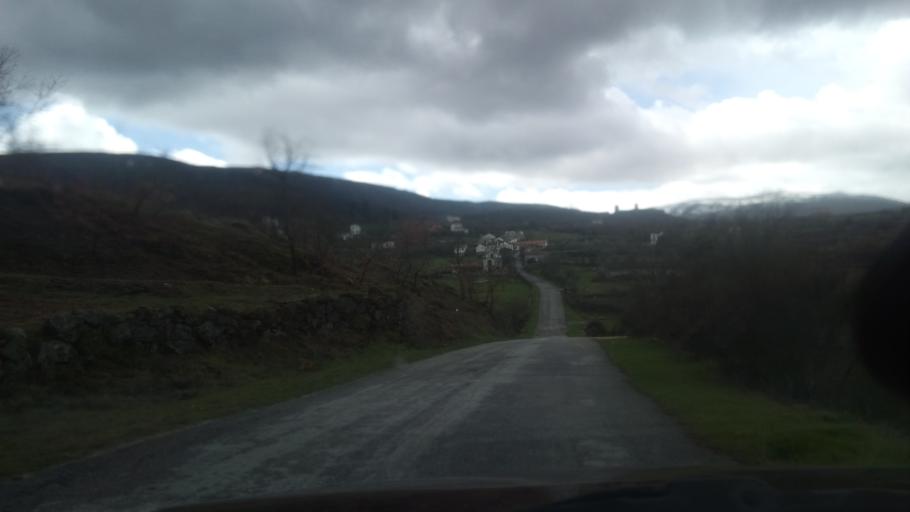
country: PT
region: Guarda
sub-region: Celorico da Beira
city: Celorico da Beira
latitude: 40.5606
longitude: -7.4568
